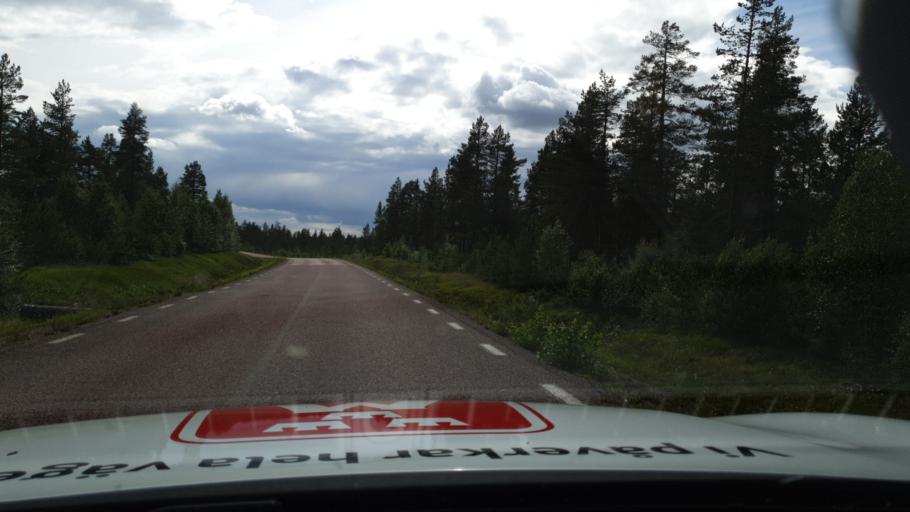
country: SE
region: Dalarna
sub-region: Alvdalens Kommun
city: AElvdalen
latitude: 61.7595
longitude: 13.4580
